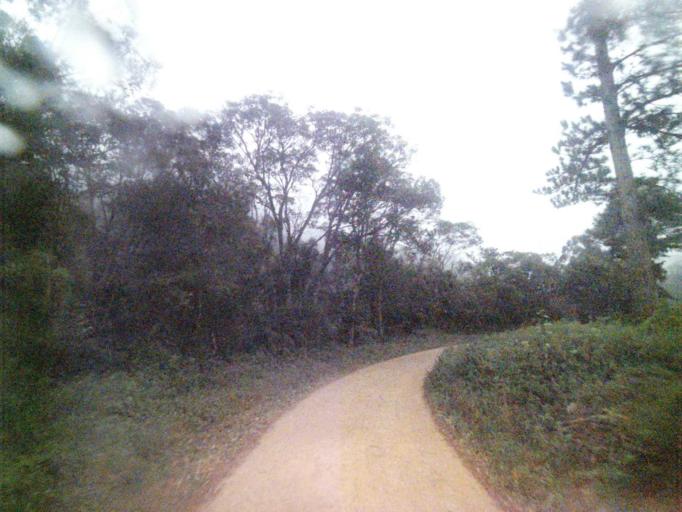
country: BR
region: Santa Catarina
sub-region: Anitapolis
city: Anitapolis
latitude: -27.8021
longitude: -49.1405
